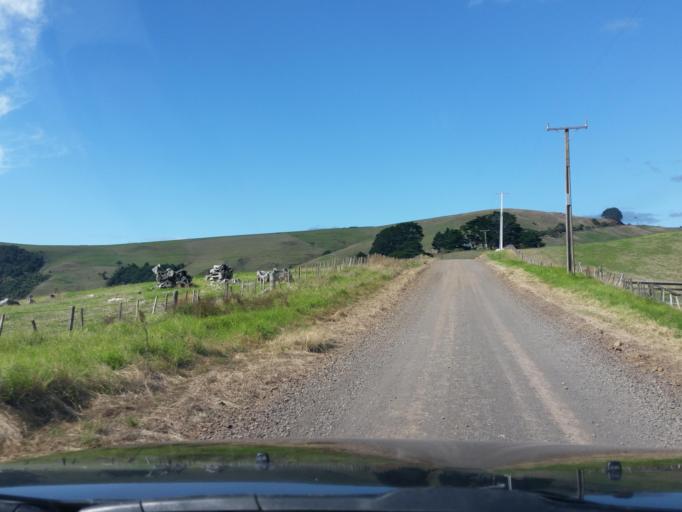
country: NZ
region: Northland
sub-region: Kaipara District
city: Dargaville
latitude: -35.7194
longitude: 173.5567
